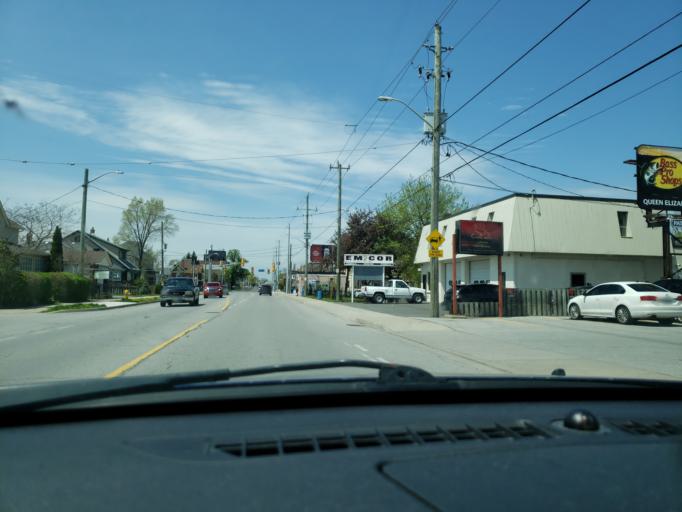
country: CA
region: Ontario
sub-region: Regional Municipality of Niagara
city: St. Catharines
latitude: 43.1614
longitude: -79.2232
